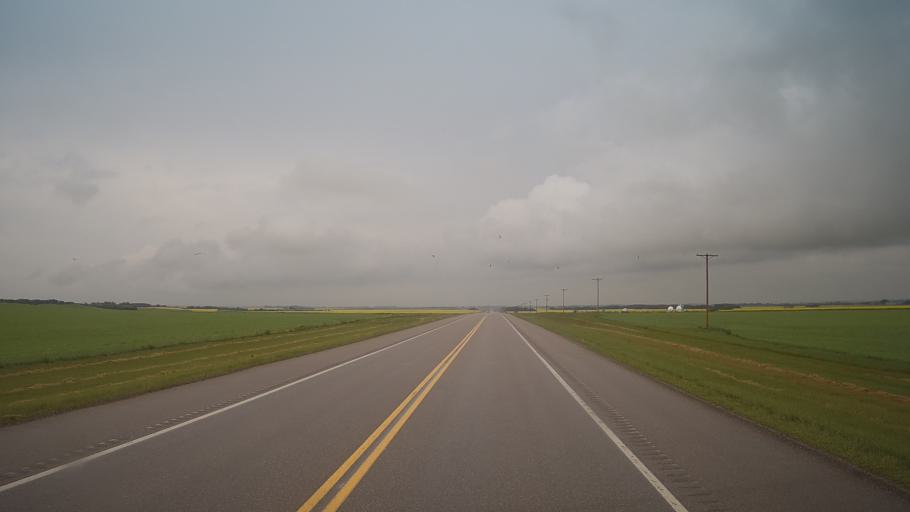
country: CA
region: Saskatchewan
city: Wilkie
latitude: 52.4178
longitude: -108.8887
